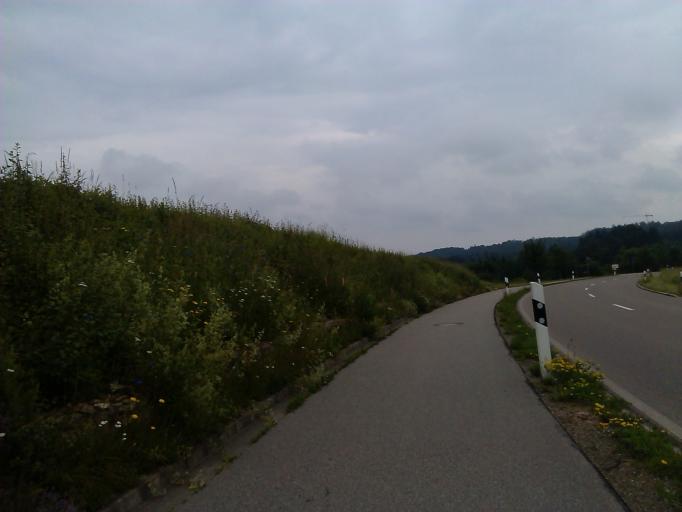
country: DE
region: Baden-Wuerttemberg
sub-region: Regierungsbezirk Stuttgart
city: Mainhardt
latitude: 49.0841
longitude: 9.5296
